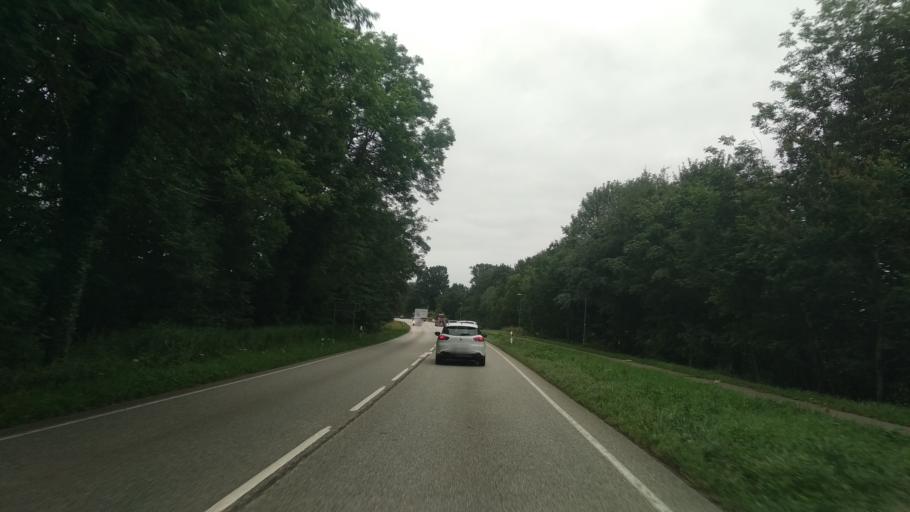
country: DE
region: Schleswig-Holstein
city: Sankelmark
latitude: 54.7209
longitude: 9.4439
